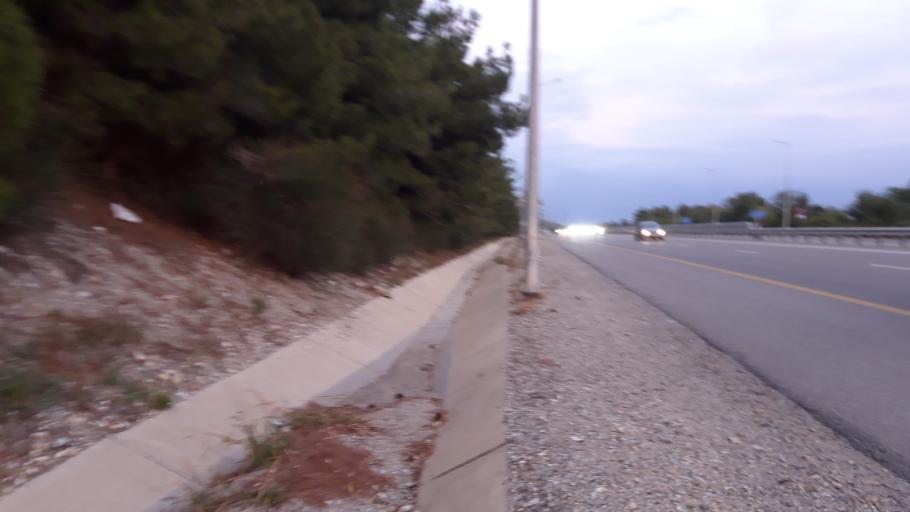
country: RU
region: Krasnodarskiy
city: Gelendzhik
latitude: 44.5788
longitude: 38.0865
